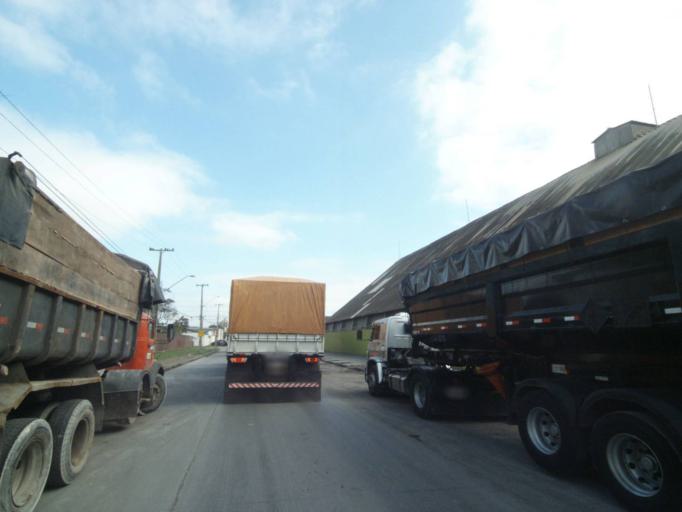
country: BR
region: Parana
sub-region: Paranagua
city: Paranagua
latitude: -25.5111
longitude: -48.5218
